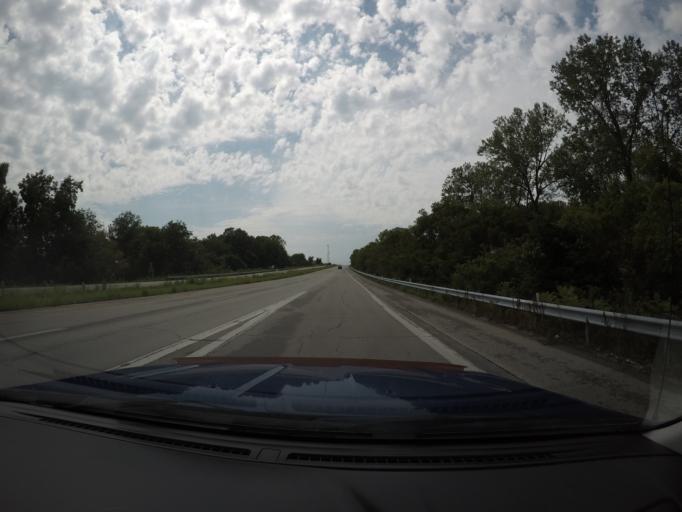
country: US
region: Missouri
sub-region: Lafayette County
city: Lexington
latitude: 39.1625
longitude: -93.8840
